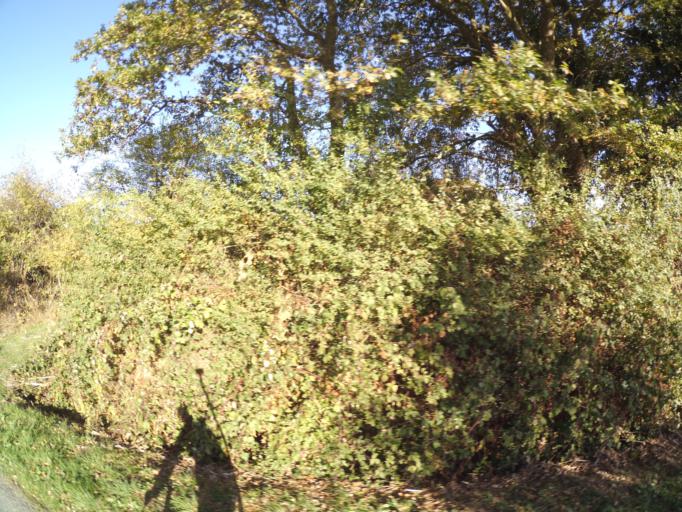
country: FR
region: Pays de la Loire
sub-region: Departement de la Loire-Atlantique
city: Saint-Lumine-de-Clisson
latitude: 47.0781
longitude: -1.3296
